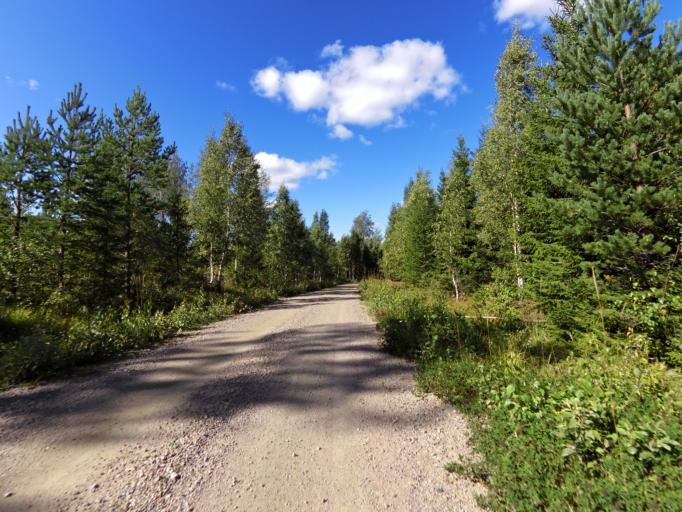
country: SE
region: Gaevleborg
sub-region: Ockelbo Kommun
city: Ockelbo
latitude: 60.7970
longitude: 16.8736
